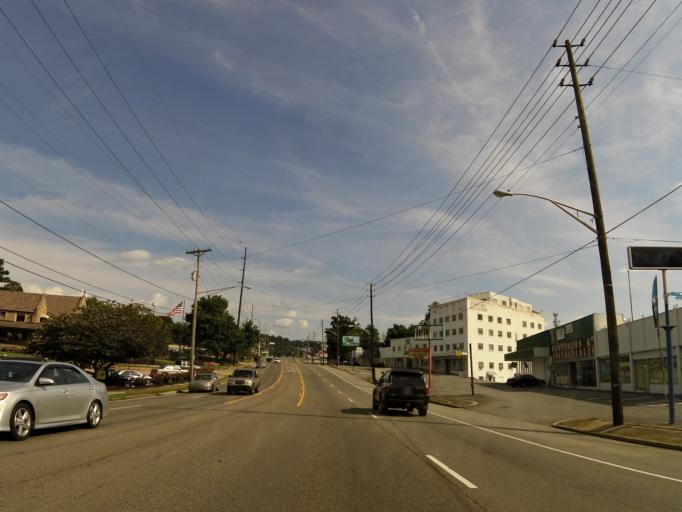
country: US
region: Tennessee
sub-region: Knox County
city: Knoxville
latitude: 35.9415
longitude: -83.9105
